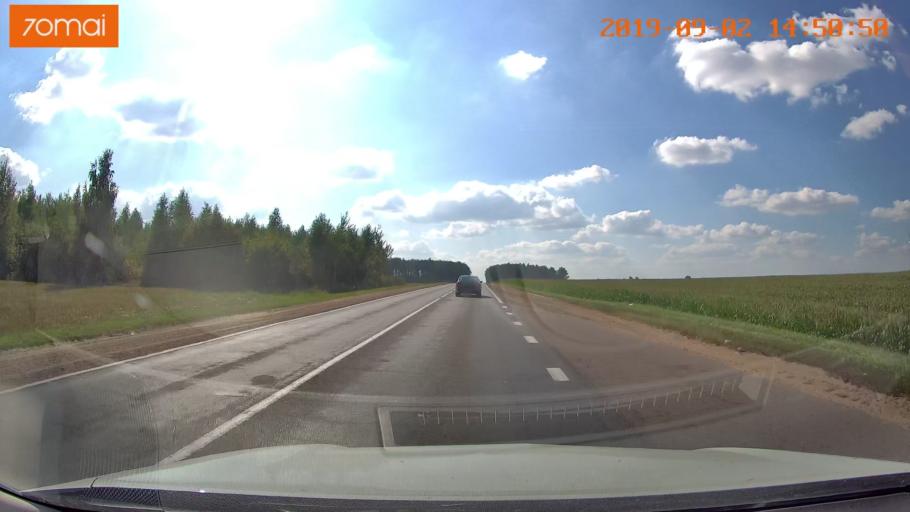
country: BY
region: Mogilev
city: Palykavichy Pyershyya
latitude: 53.9789
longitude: 30.3009
